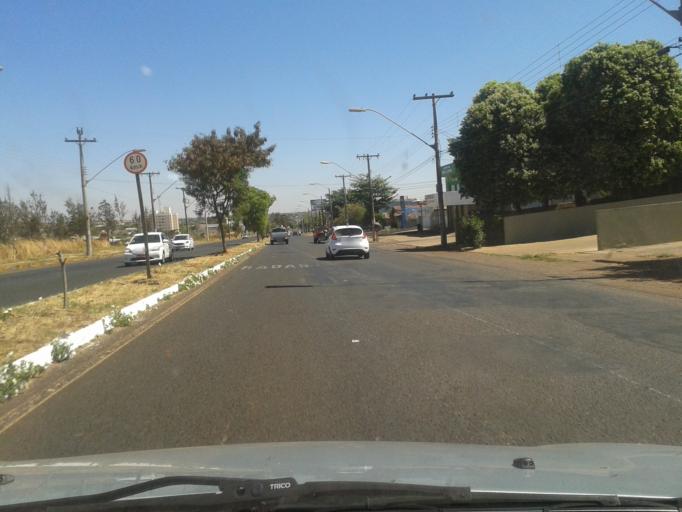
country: BR
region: Minas Gerais
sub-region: Uberlandia
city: Uberlandia
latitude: -18.8805
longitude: -48.2717
